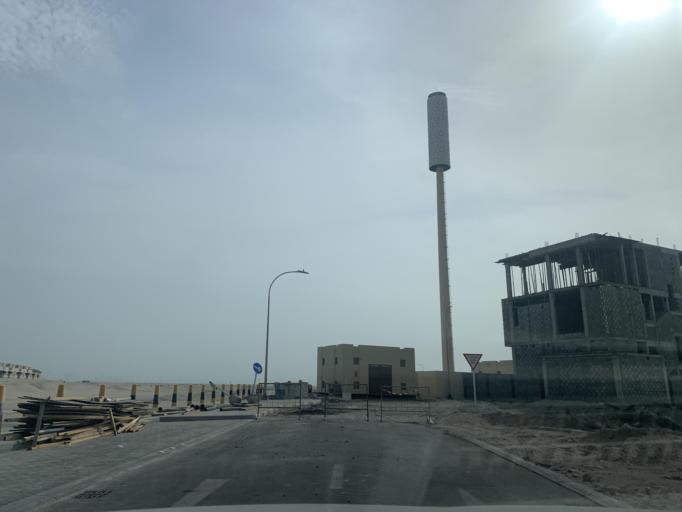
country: BH
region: Muharraq
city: Al Muharraq
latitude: 26.3182
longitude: 50.6218
